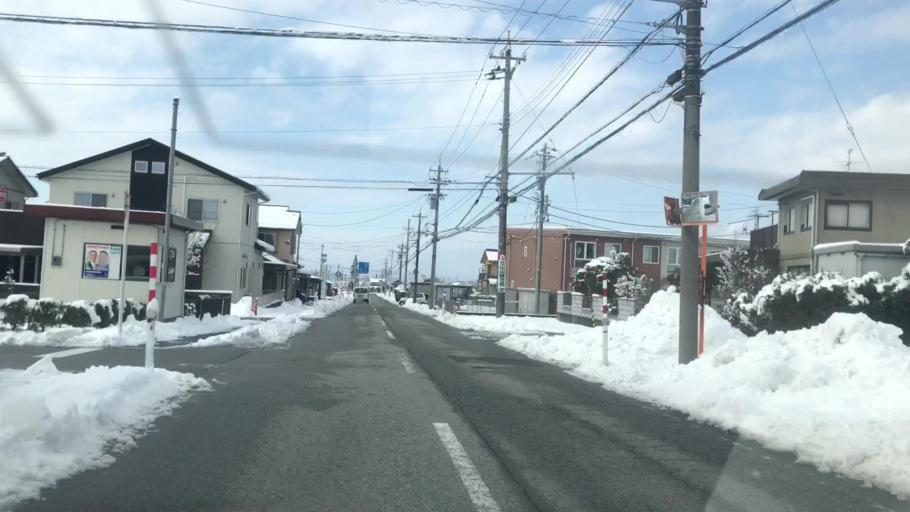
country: JP
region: Toyama
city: Toyama-shi
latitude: 36.6168
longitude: 137.2738
